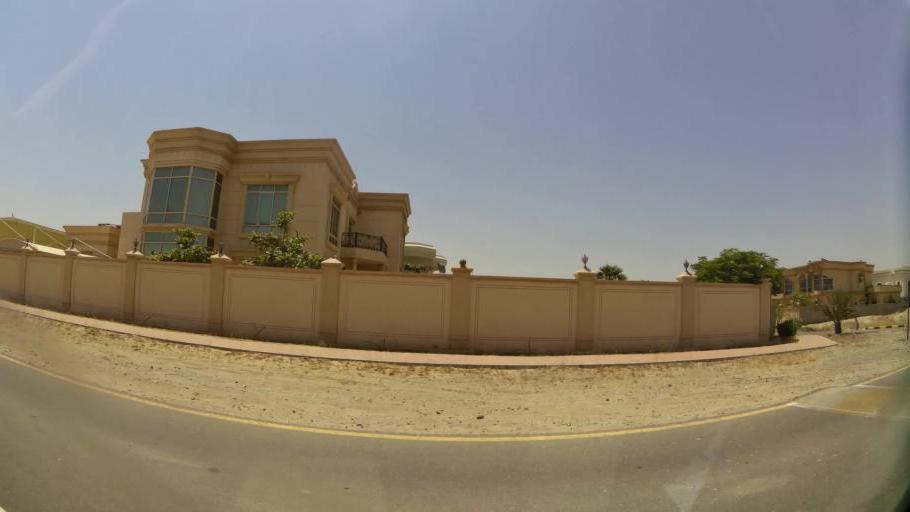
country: AE
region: Ajman
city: Ajman
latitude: 25.4256
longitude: 55.5144
